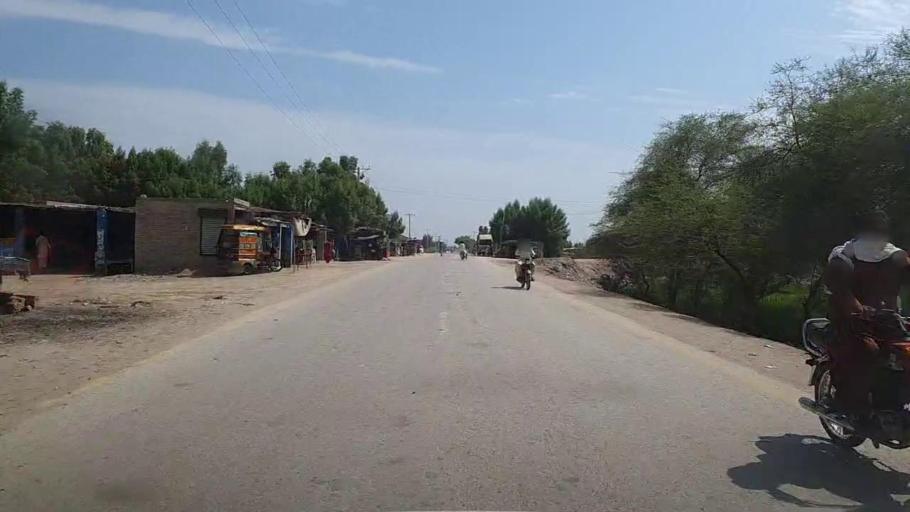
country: PK
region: Sindh
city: Thul
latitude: 28.2382
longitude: 68.7896
